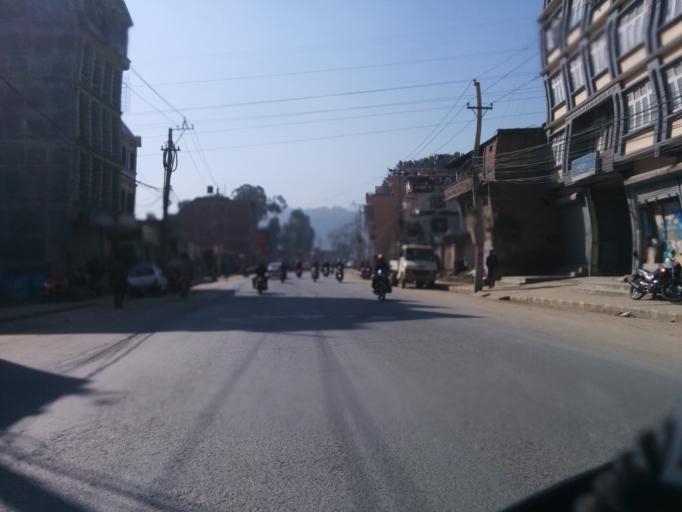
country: NP
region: Central Region
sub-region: Bagmati Zone
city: Patan
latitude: 27.6807
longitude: 85.2982
